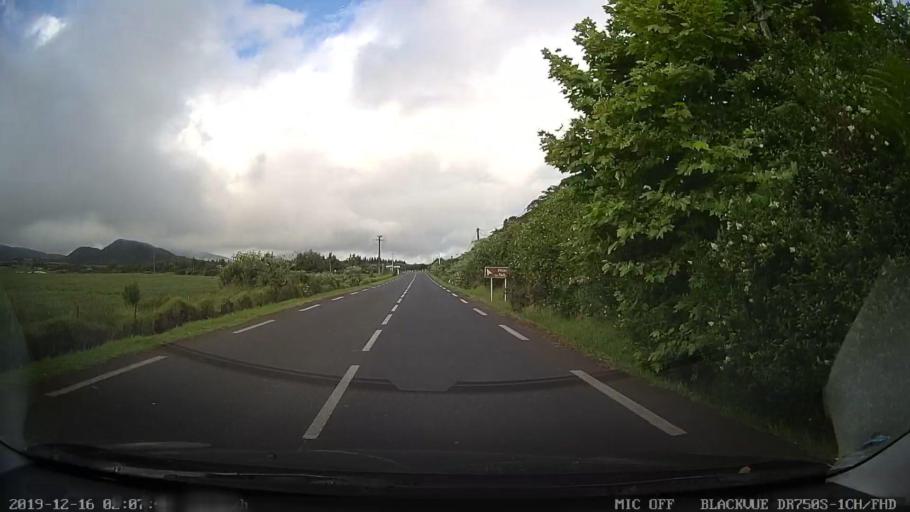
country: RE
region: Reunion
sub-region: Reunion
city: Cilaos
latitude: -21.1771
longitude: 55.5804
